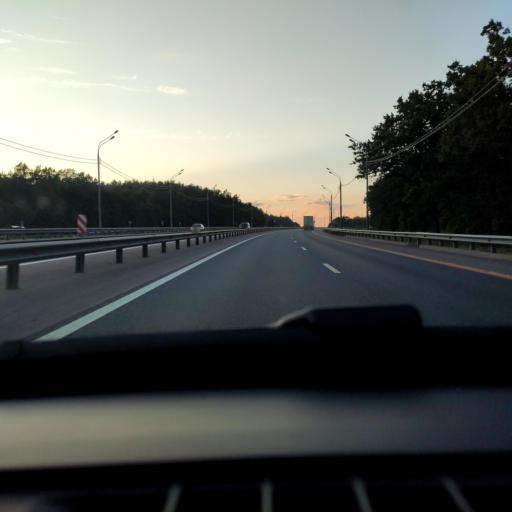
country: RU
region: Lipetsk
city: Khlevnoye
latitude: 52.2432
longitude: 39.0671
